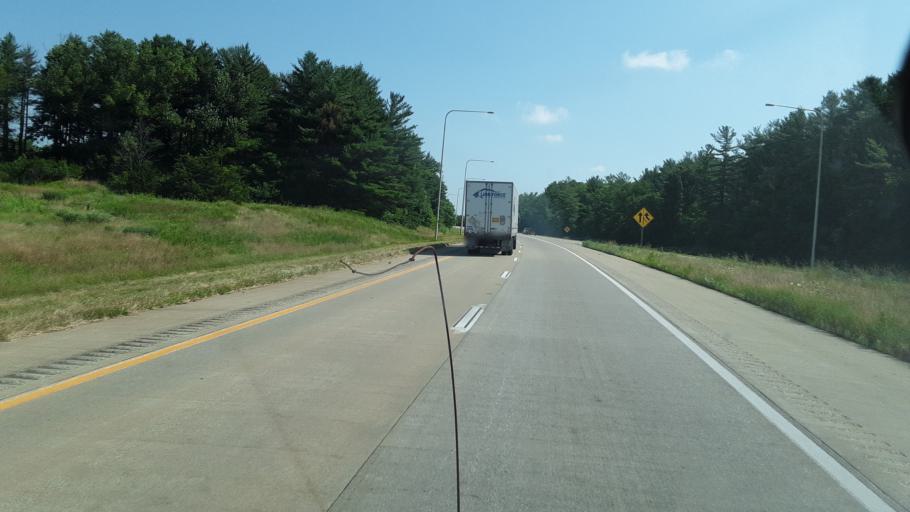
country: US
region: Illinois
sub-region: Effingham County
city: Effingham
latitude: 39.0961
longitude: -88.5784
